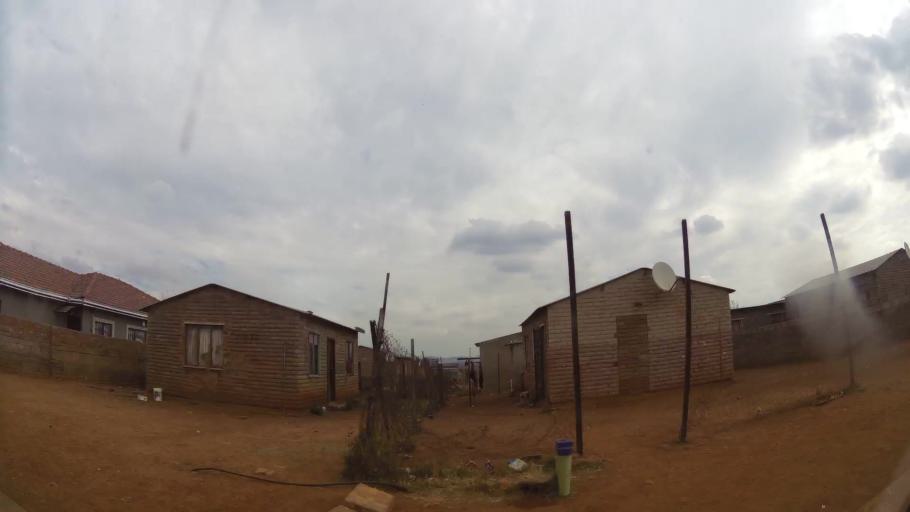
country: ZA
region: Gauteng
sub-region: Ekurhuleni Metropolitan Municipality
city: Germiston
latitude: -26.3844
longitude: 28.1214
